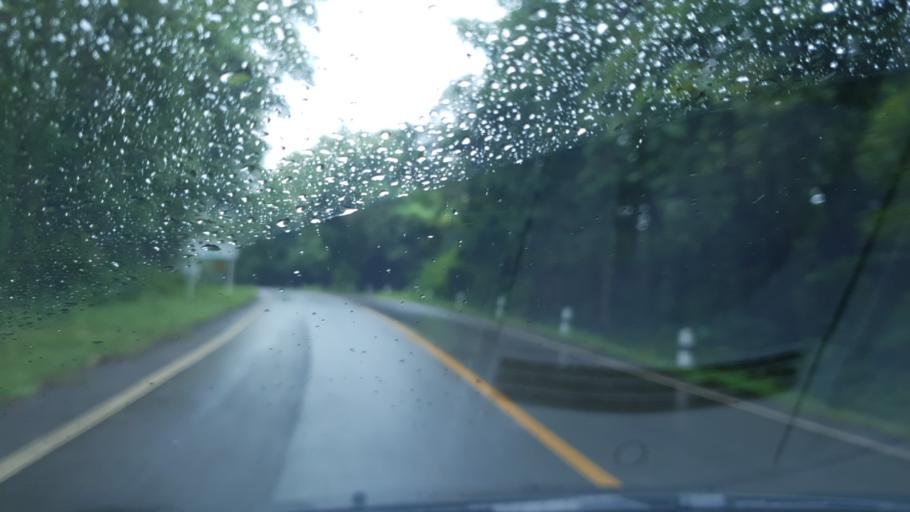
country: TH
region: Mae Hong Son
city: Mae La Noi
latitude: 18.5379
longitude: 97.9372
